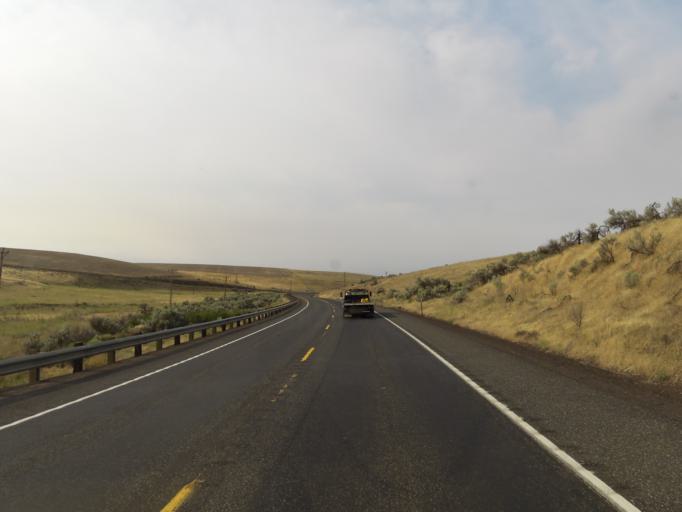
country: US
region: Oregon
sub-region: Sherman County
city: Moro
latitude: 45.4992
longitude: -120.7068
